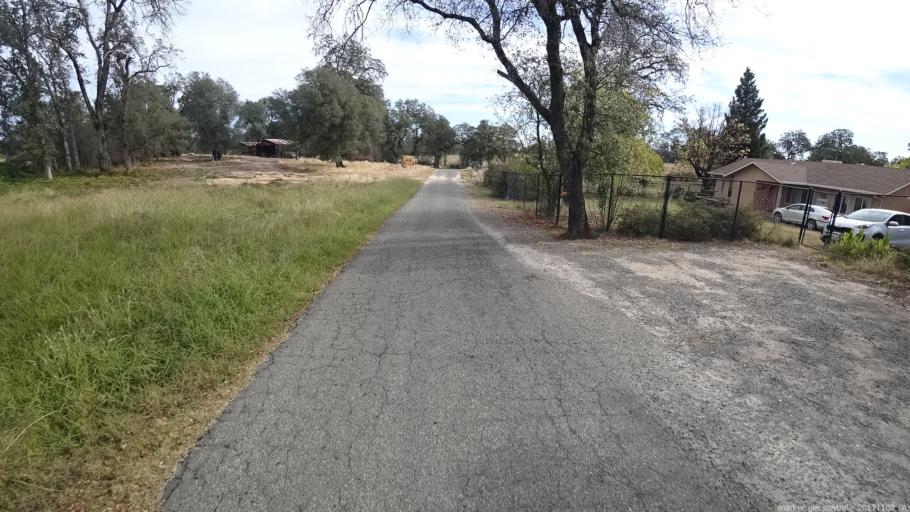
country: US
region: California
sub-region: Shasta County
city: Shasta
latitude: 40.5013
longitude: -122.5821
